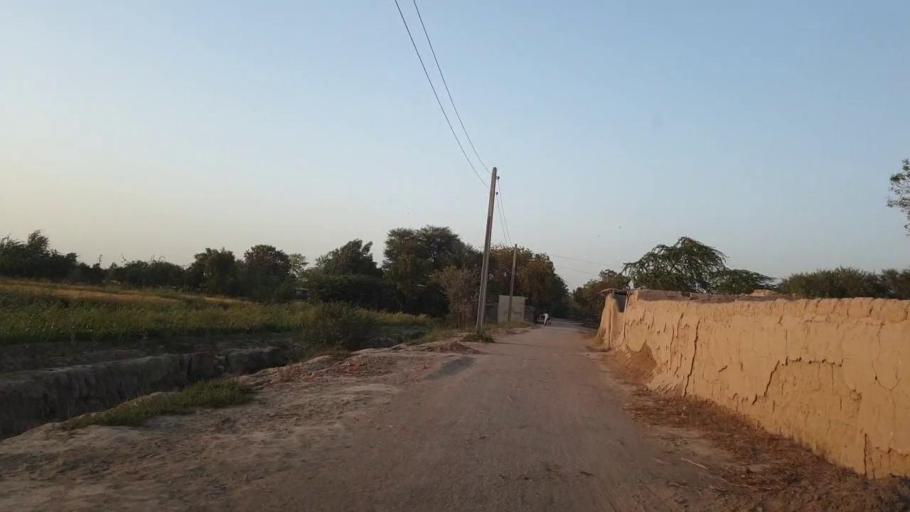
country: PK
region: Sindh
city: Tando Ghulam Ali
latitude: 25.1333
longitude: 68.9149
